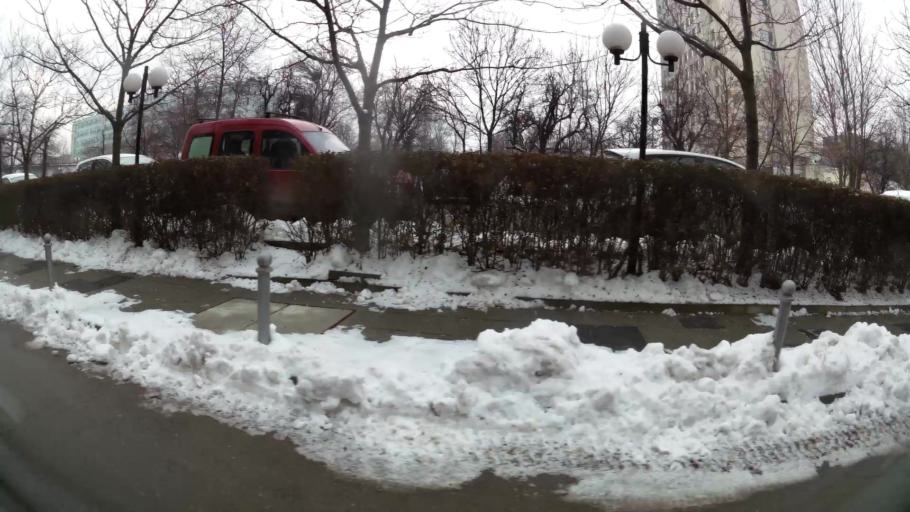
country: BG
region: Sofia-Capital
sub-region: Stolichna Obshtina
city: Sofia
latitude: 42.7179
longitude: 23.2970
